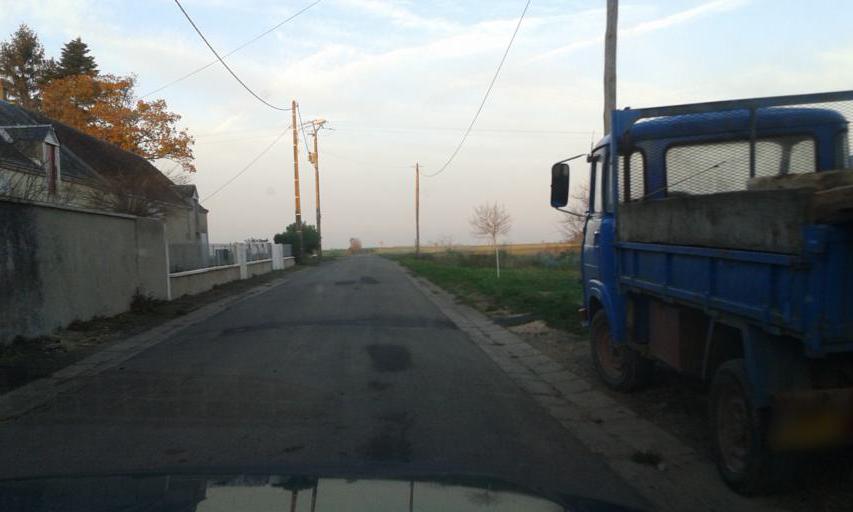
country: FR
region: Centre
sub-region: Departement du Loiret
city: Tavers
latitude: 47.7732
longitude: 1.5478
